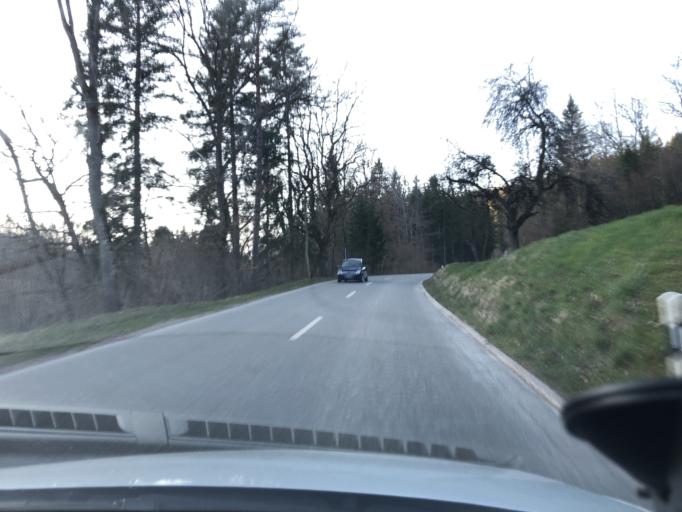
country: DE
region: Baden-Wuerttemberg
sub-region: Freiburg Region
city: Braunlingen
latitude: 47.8490
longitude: 8.4498
